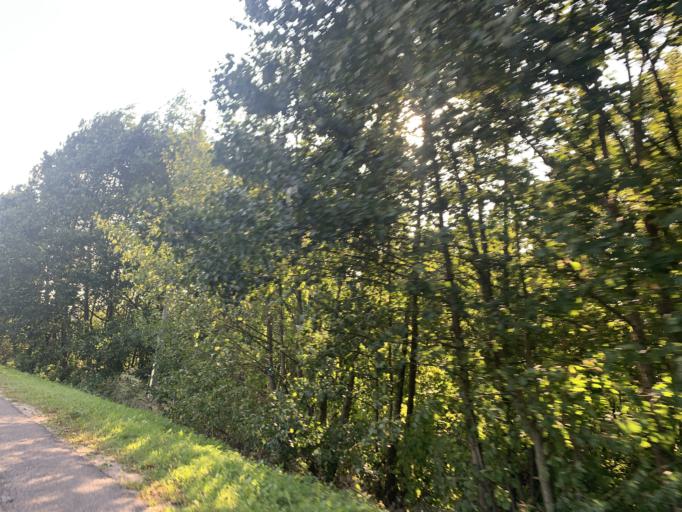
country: BY
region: Minsk
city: Ivyanyets
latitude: 53.8824
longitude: 26.7433
